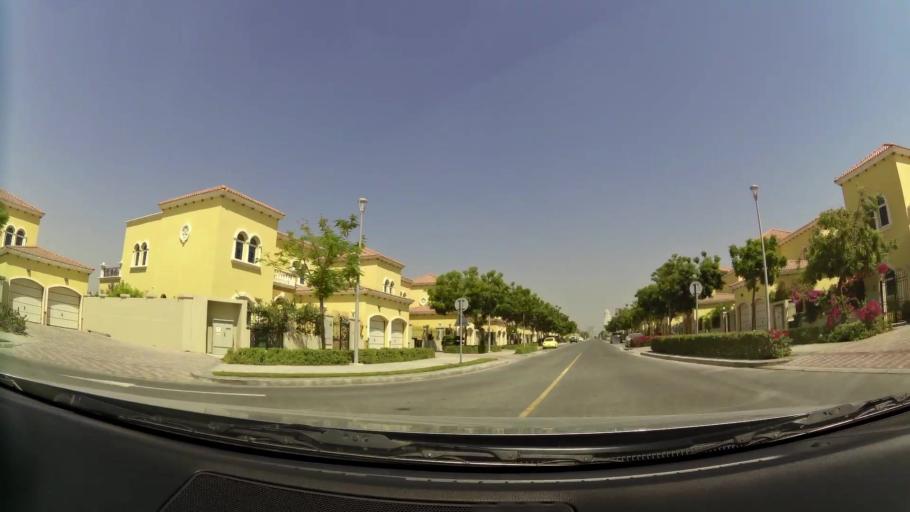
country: AE
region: Dubai
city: Dubai
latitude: 25.0488
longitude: 55.1539
